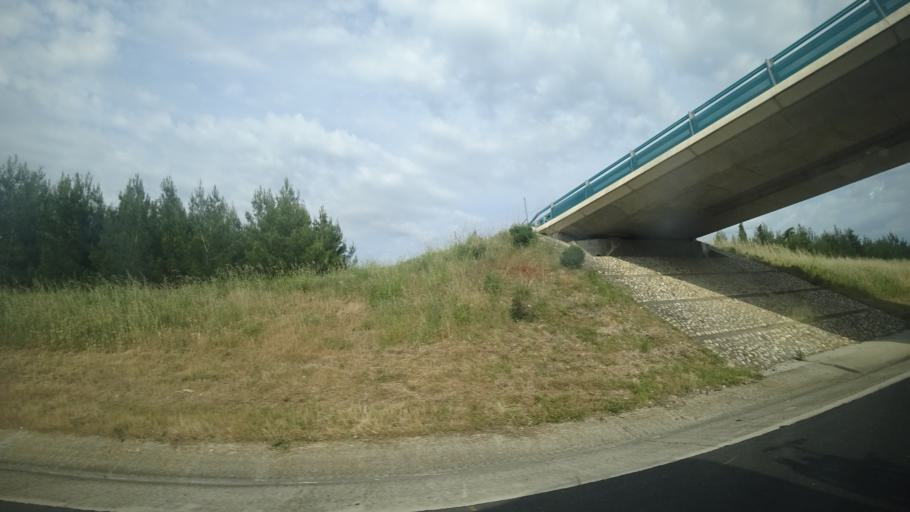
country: FR
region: Languedoc-Roussillon
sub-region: Departement de l'Herault
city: Aspiran
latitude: 43.5693
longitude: 3.4646
